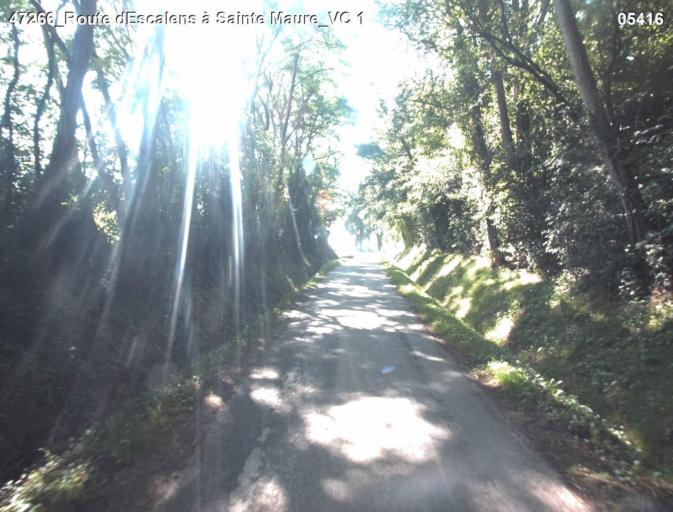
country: FR
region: Midi-Pyrenees
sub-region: Departement du Gers
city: Montreal
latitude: 44.0131
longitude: 0.1214
